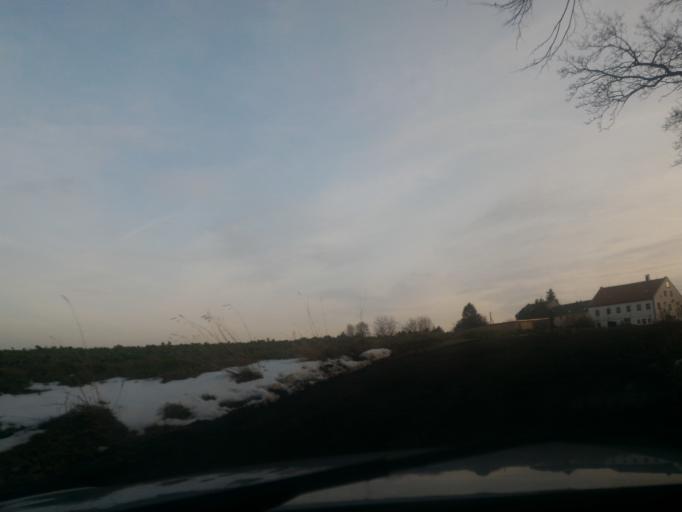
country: DE
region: Saxony
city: Olbersdorf
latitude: 50.8732
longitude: 14.7774
